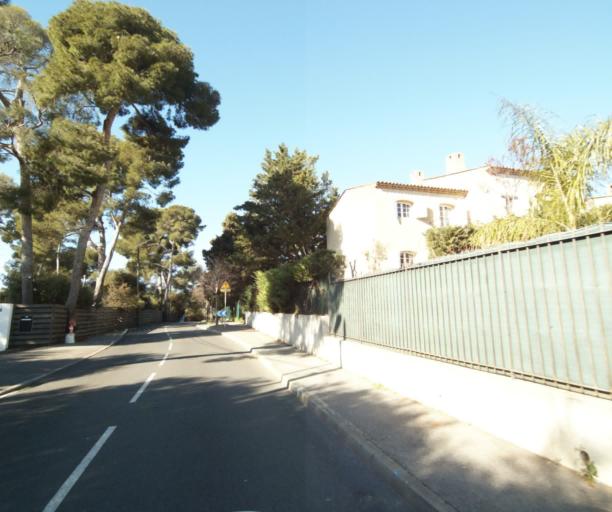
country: FR
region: Provence-Alpes-Cote d'Azur
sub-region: Departement des Alpes-Maritimes
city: Biot
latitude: 43.6039
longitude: 7.0978
